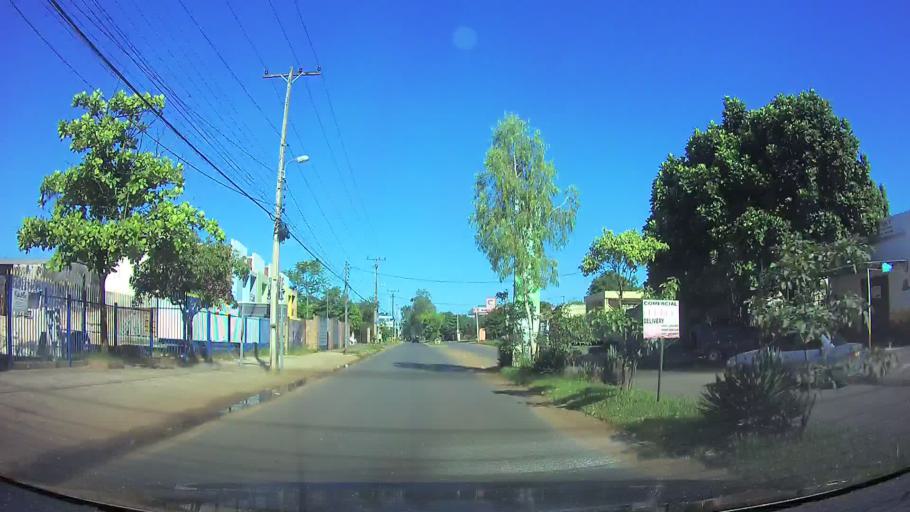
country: PY
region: Central
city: Fernando de la Mora
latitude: -25.2964
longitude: -57.5190
